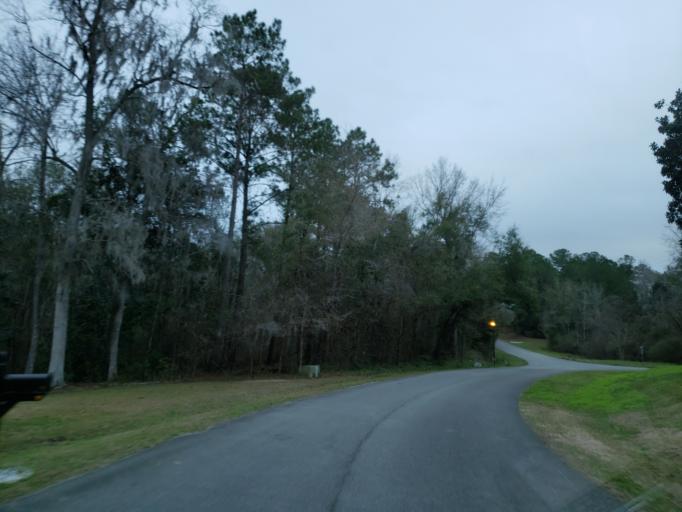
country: US
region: Georgia
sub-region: Lowndes County
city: Remerton
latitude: 30.8972
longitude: -83.3639
